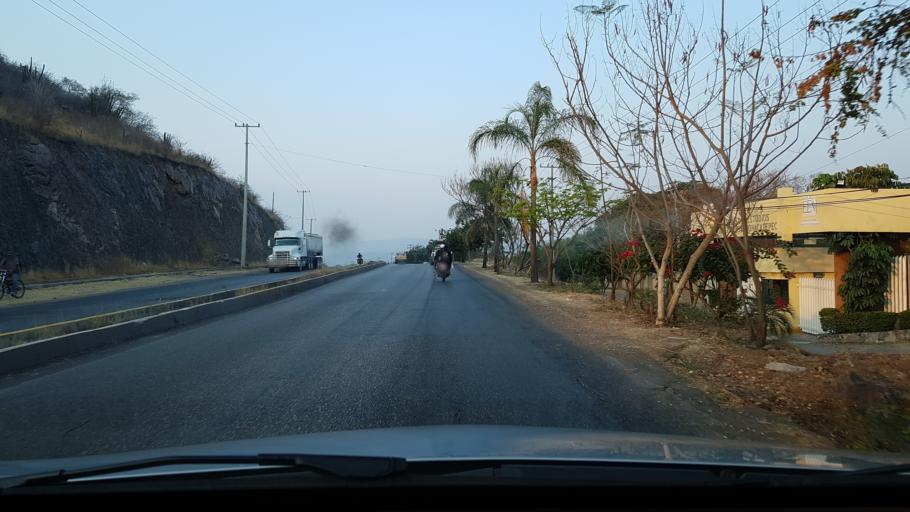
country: MX
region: Morelos
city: Jonacatepec de Leandro Valle
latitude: 18.6673
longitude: -98.8076
